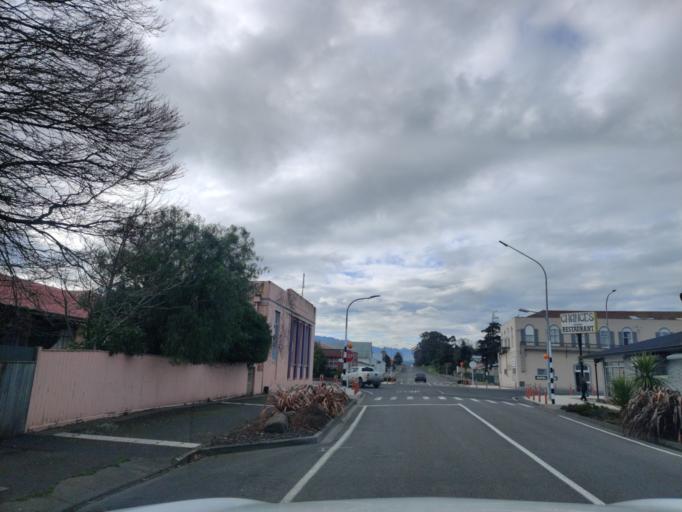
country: NZ
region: Manawatu-Wanganui
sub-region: Palmerston North City
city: Palmerston North
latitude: -40.3376
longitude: 175.8665
